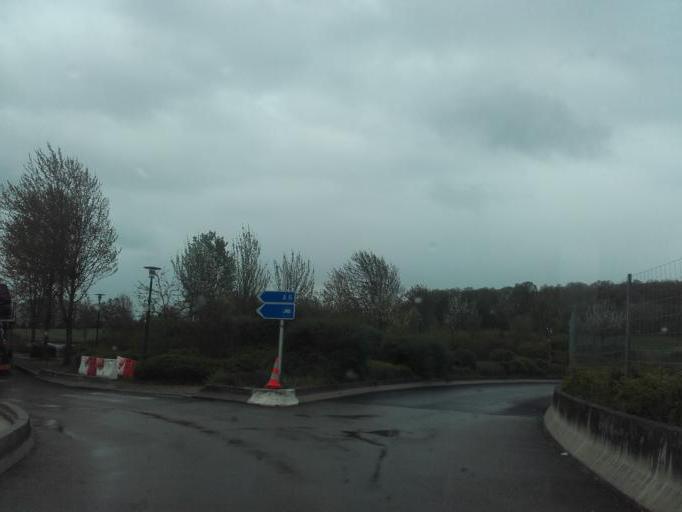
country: FR
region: Bourgogne
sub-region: Departement de l'Yonne
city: Avallon
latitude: 47.5027
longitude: 4.0363
